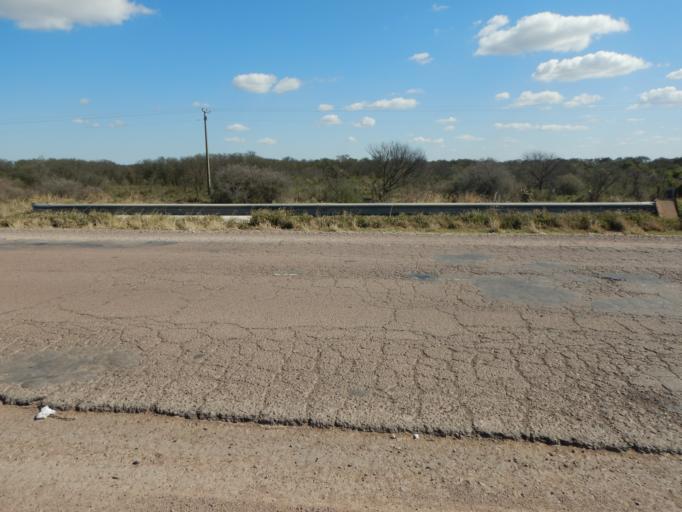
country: AR
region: Santiago del Estero
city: Los Juries
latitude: -28.6604
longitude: -61.5285
